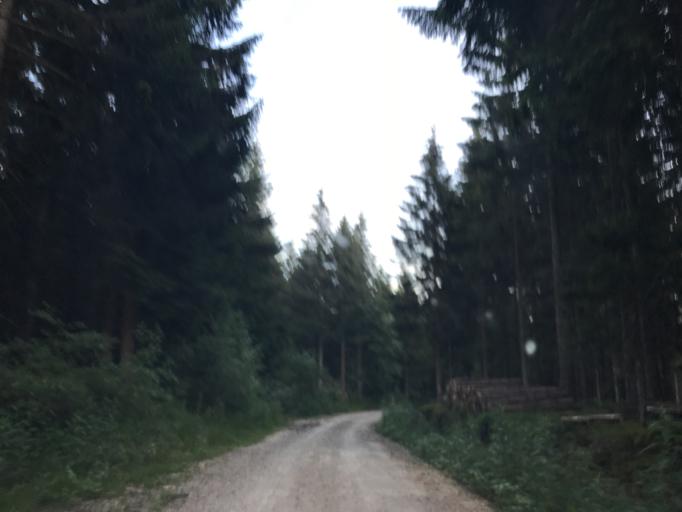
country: FR
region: Rhone-Alpes
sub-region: Departement de la Loire
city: Noiretable
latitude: 45.8063
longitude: 3.6948
